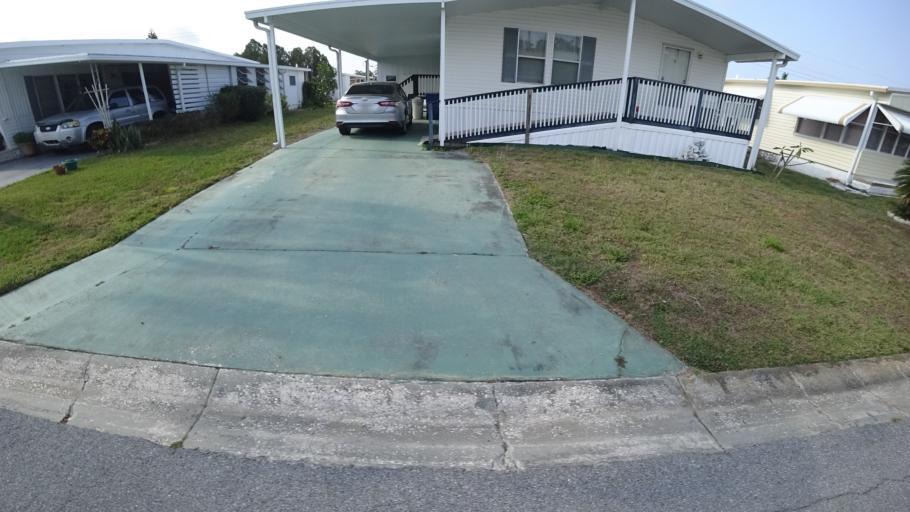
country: US
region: Florida
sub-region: Manatee County
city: West Samoset
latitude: 27.4528
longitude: -82.5640
